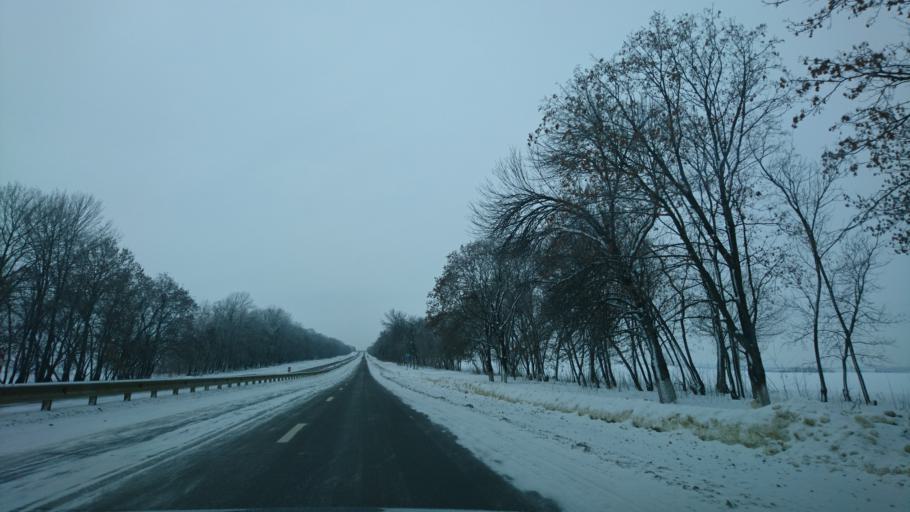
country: RU
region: Belgorod
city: Mayskiy
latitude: 50.4323
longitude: 36.3869
